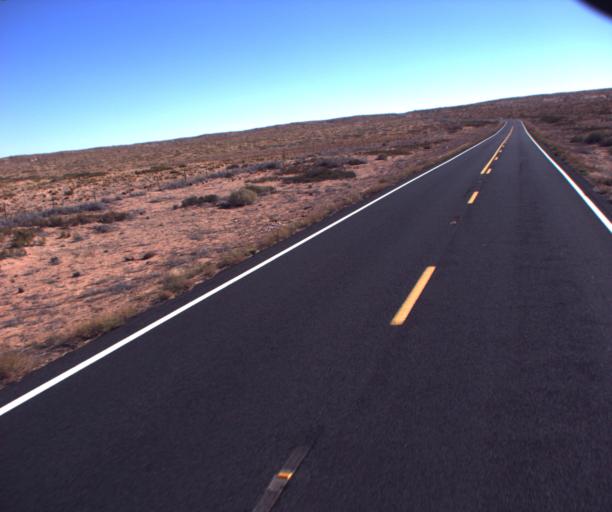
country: US
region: Arizona
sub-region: Coconino County
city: Tuba City
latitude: 36.0221
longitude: -111.1349
